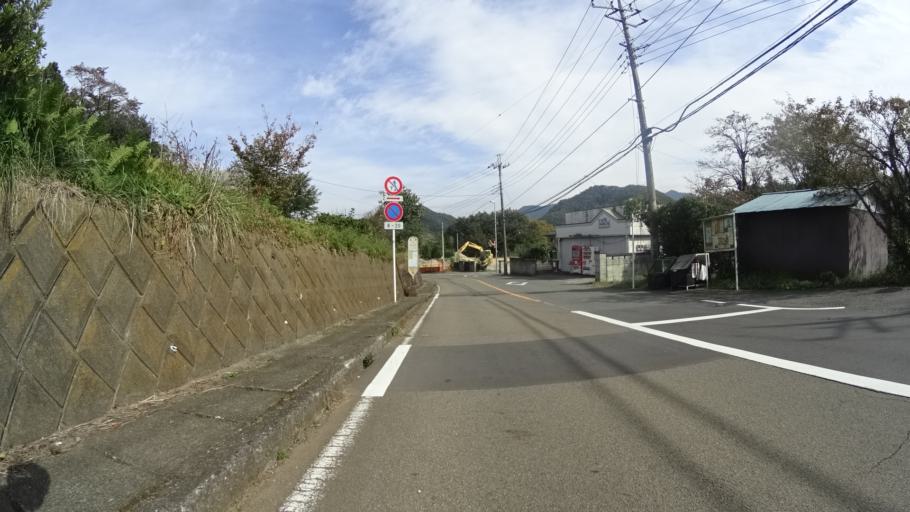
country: JP
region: Yamanashi
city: Uenohara
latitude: 35.5871
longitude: 139.1471
